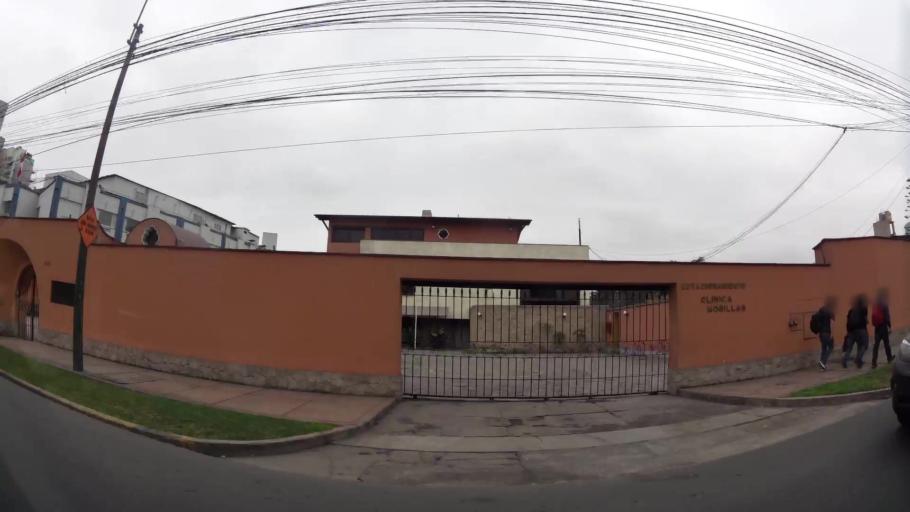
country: PE
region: Lima
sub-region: Lima
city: La Molina
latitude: -12.1031
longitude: -76.9725
